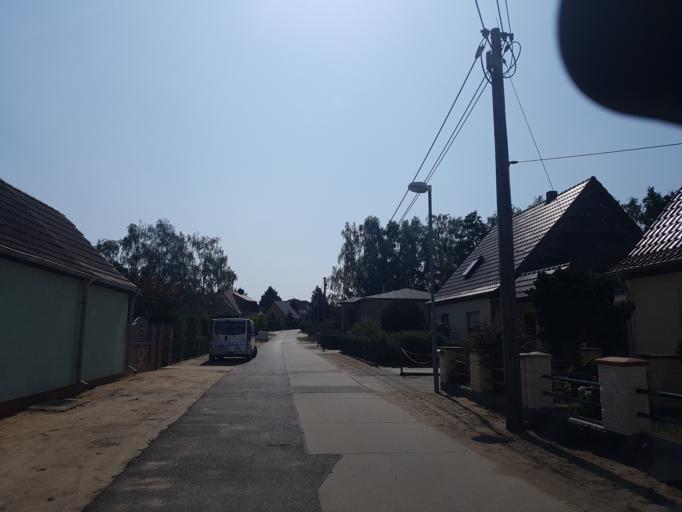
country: DE
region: Brandenburg
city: Treuenbrietzen
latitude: 52.0899
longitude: 12.8442
